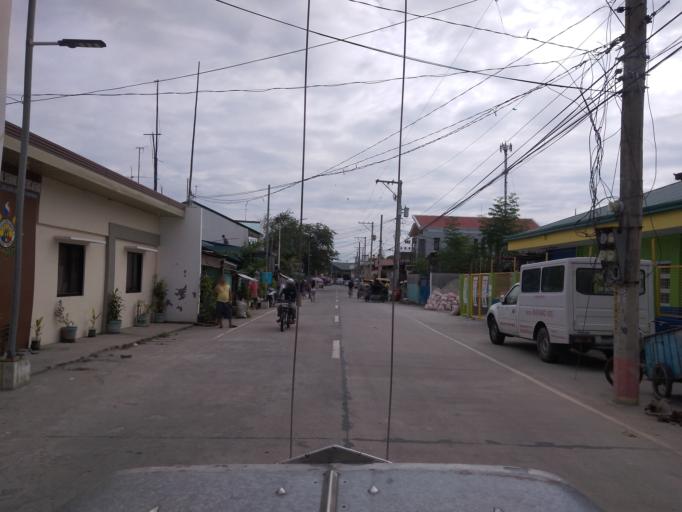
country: PH
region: Central Luzon
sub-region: Province of Pampanga
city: Sexmoan
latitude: 14.9368
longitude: 120.6203
